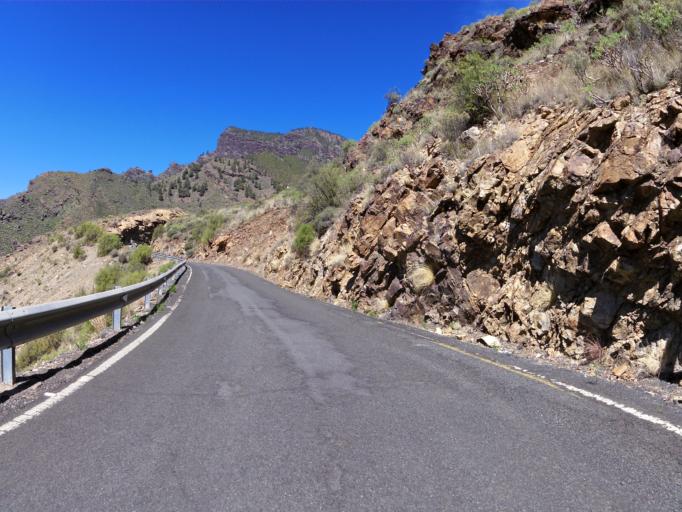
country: ES
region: Canary Islands
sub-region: Provincia de Las Palmas
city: Artenara
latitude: 27.9950
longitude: -15.6932
